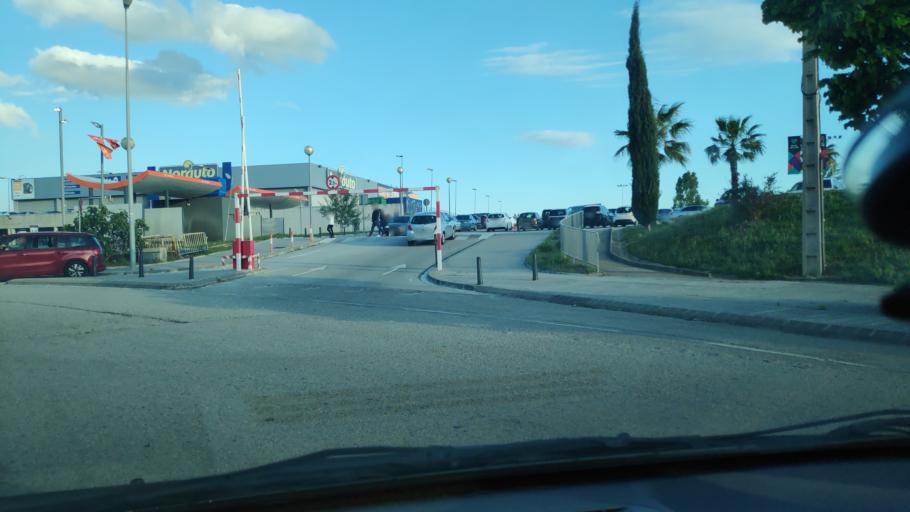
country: ES
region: Catalonia
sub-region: Provincia de Barcelona
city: Terrassa
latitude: 41.5448
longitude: 2.0242
